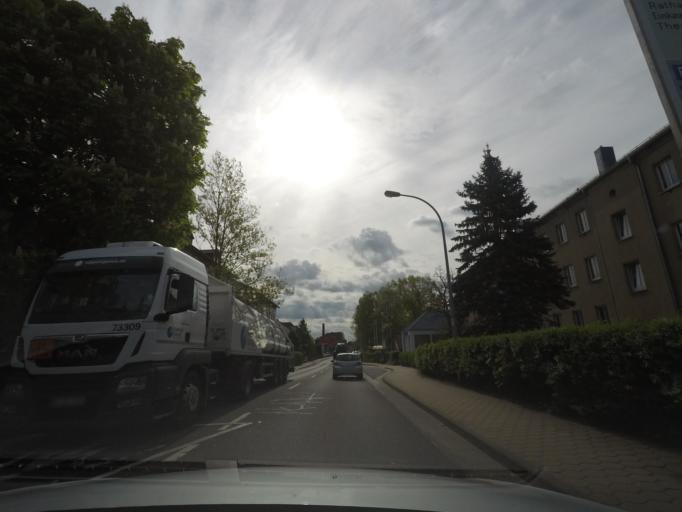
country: DE
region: Saxony
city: Dobeln
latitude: 51.1248
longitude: 13.0957
